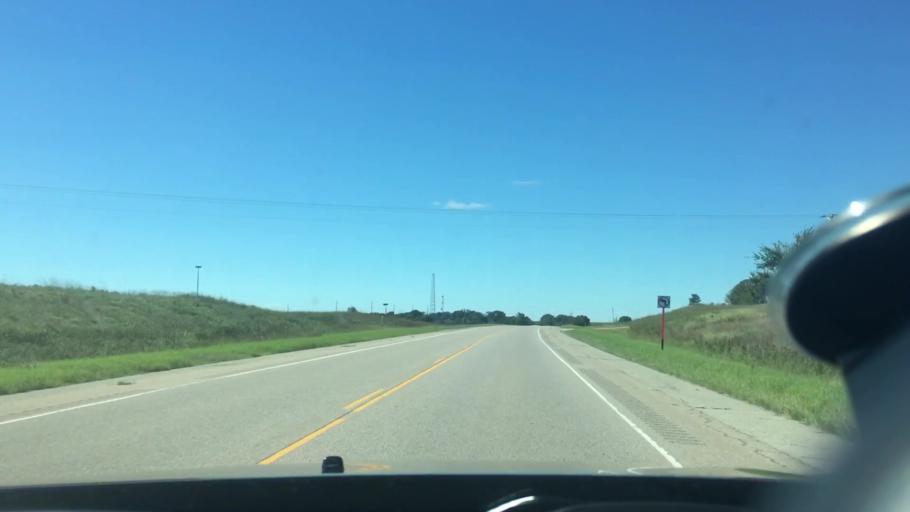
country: US
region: Oklahoma
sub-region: Coal County
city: Coalgate
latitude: 34.6136
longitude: -96.4405
